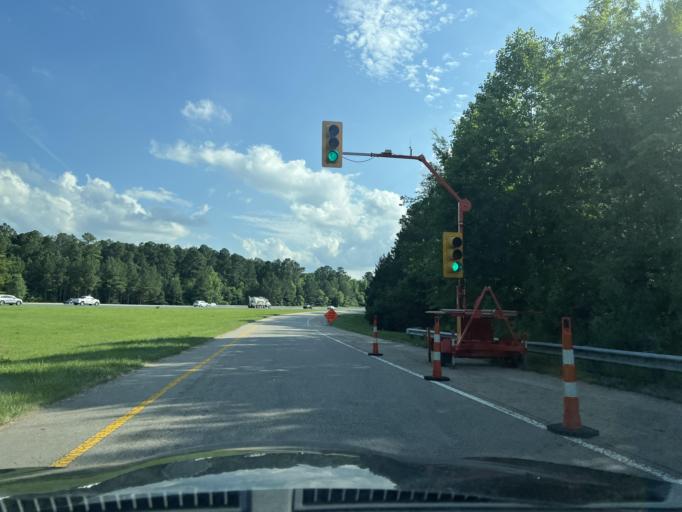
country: US
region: North Carolina
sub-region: Wake County
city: Morrisville
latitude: 35.8977
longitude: -78.7883
